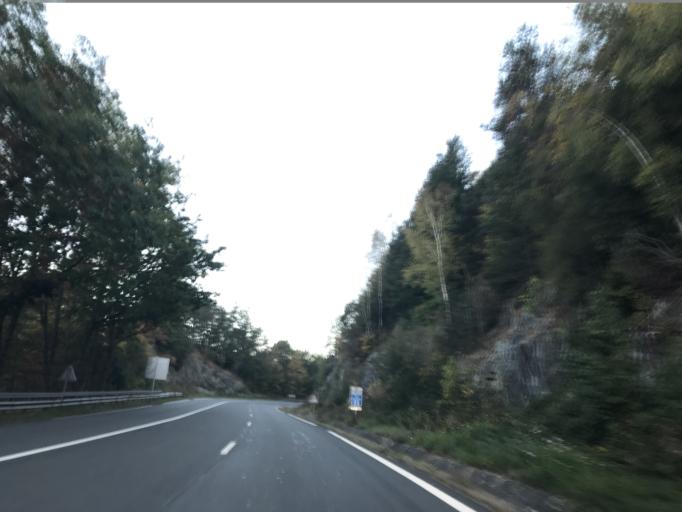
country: FR
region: Auvergne
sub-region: Departement du Puy-de-Dome
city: Celles-sur-Durolle
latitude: 45.8713
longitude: 3.6278
